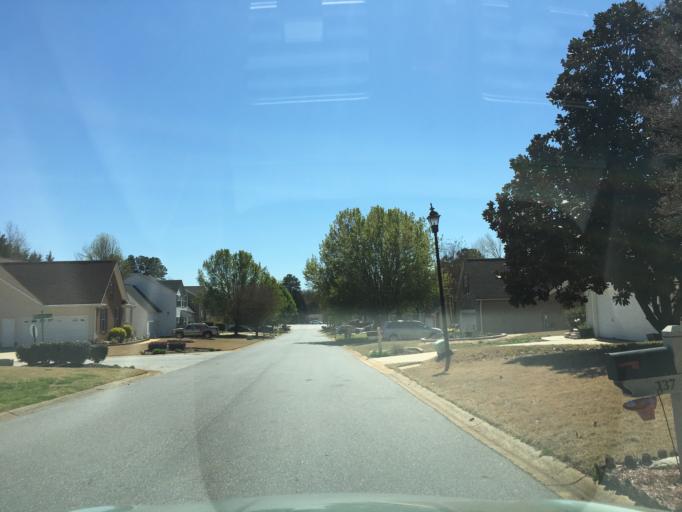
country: US
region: South Carolina
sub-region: Spartanburg County
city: Roebuck
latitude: 34.8793
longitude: -82.0441
